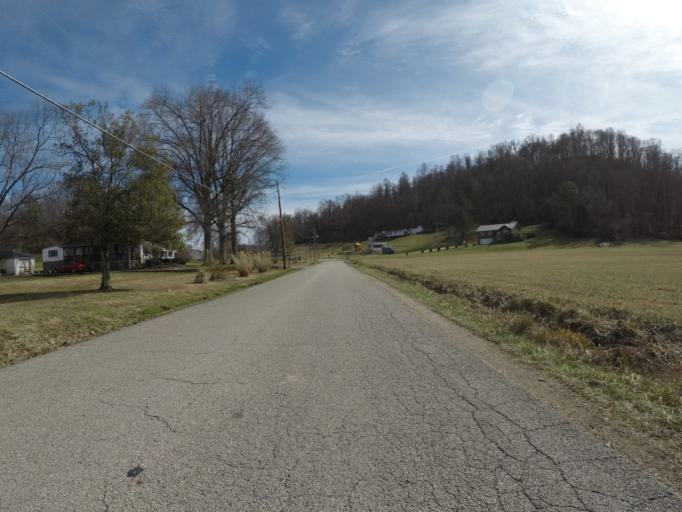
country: US
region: Ohio
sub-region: Lawrence County
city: Burlington
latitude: 38.3497
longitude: -82.5103
